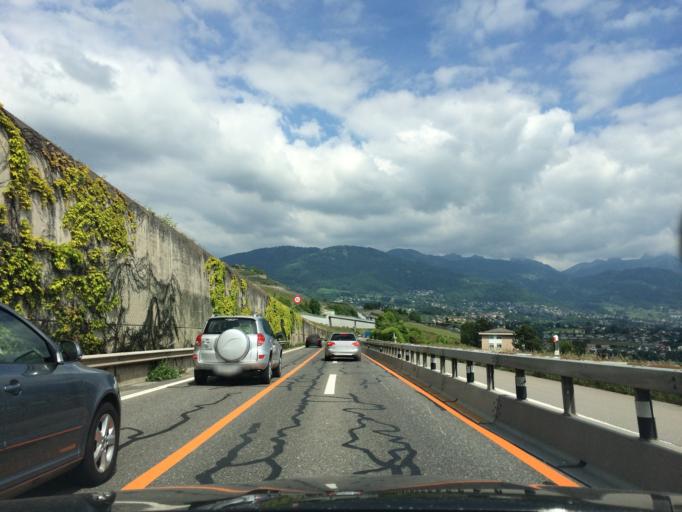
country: CH
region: Vaud
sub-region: Riviera-Pays-d'Enhaut District
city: Chardonne
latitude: 46.4742
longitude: 6.8275
